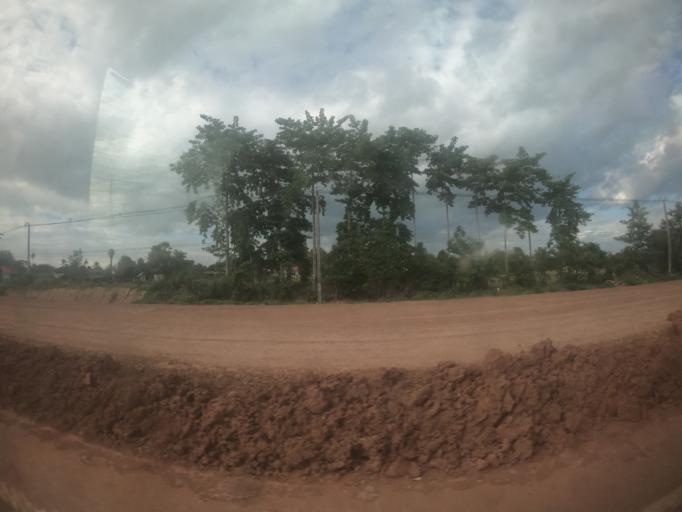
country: TH
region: Surin
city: Kap Choeng
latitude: 14.5054
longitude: 103.5583
